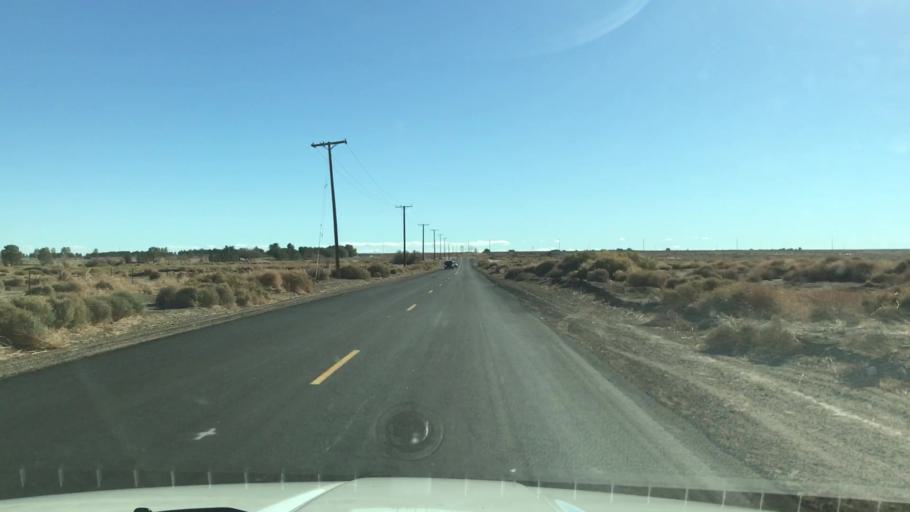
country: US
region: California
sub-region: Kern County
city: California City
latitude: 35.2772
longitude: -117.9857
